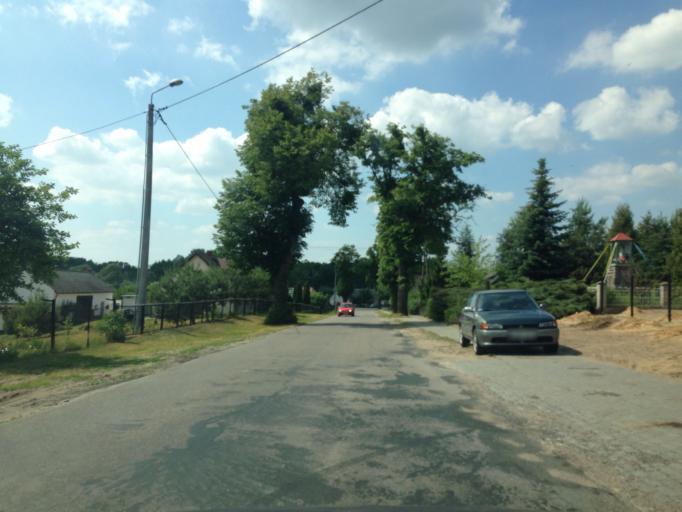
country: PL
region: Kujawsko-Pomorskie
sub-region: Powiat brodnicki
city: Bartniczka
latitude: 53.2404
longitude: 19.6169
